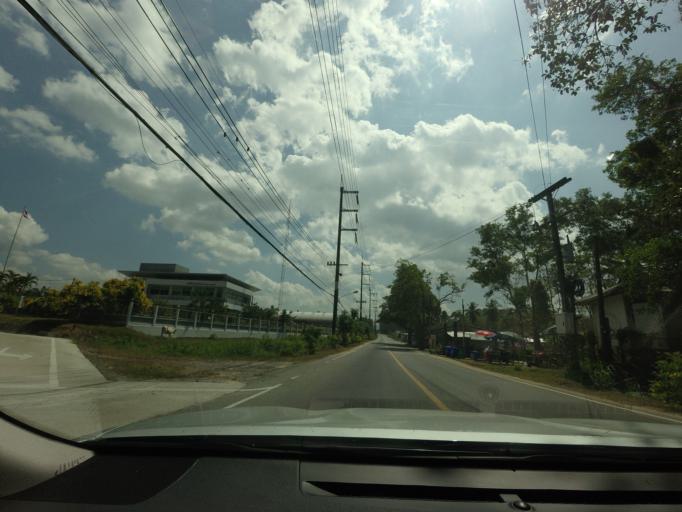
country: TH
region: Phangnga
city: Thai Mueang
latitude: 8.3973
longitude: 98.2606
